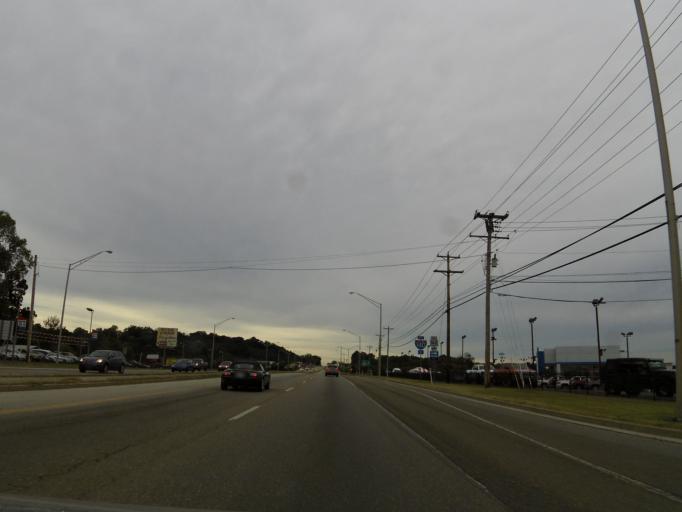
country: US
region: Tennessee
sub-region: Blount County
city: Alcoa
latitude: 35.8322
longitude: -83.9728
